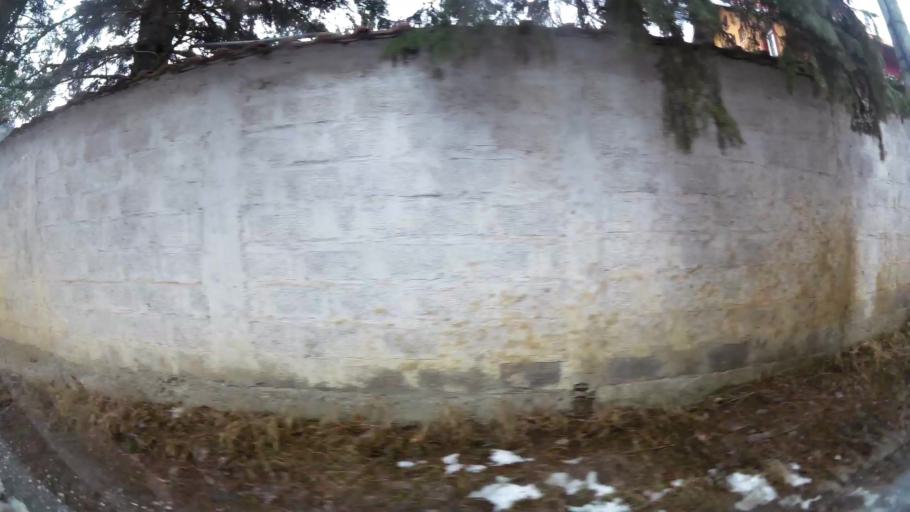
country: BG
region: Sofiya
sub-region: Obshtina Bozhurishte
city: Bozhurishte
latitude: 42.6705
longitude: 23.2348
